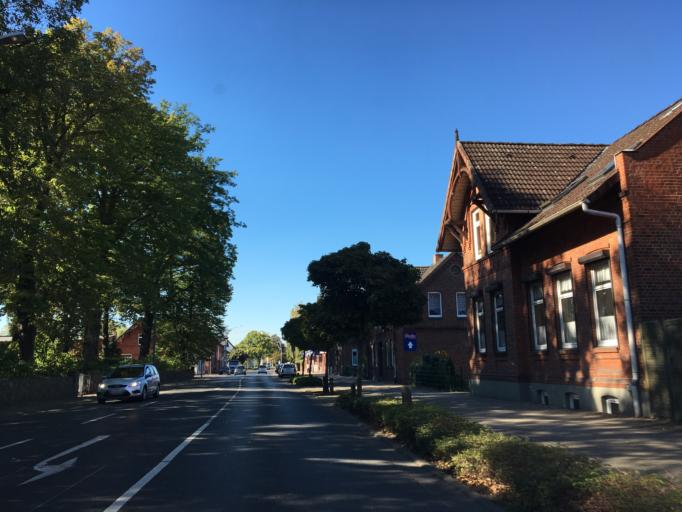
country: DE
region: Lower Saxony
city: Winsen
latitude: 53.3555
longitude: 10.2097
